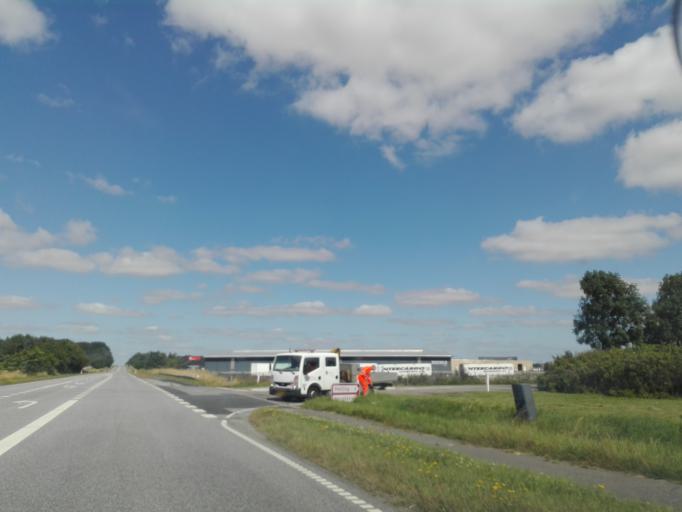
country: DK
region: Central Jutland
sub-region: Favrskov Kommune
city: Hadsten
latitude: 56.3295
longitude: 10.1203
